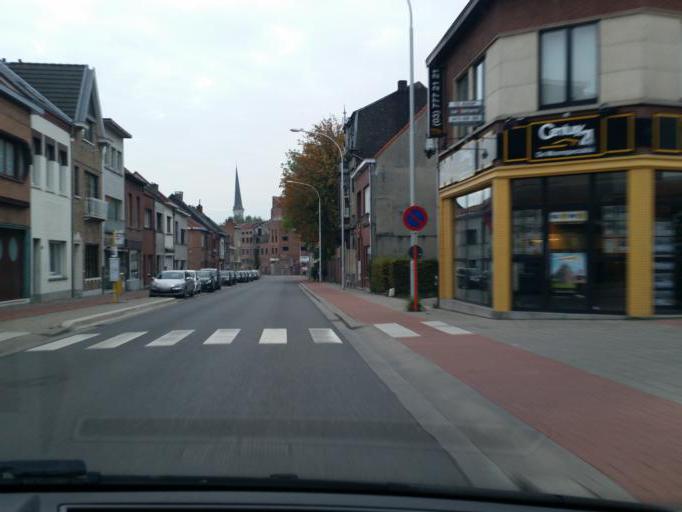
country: BE
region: Flanders
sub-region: Provincie Antwerpen
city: Schelle
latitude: 51.1325
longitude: 4.3354
